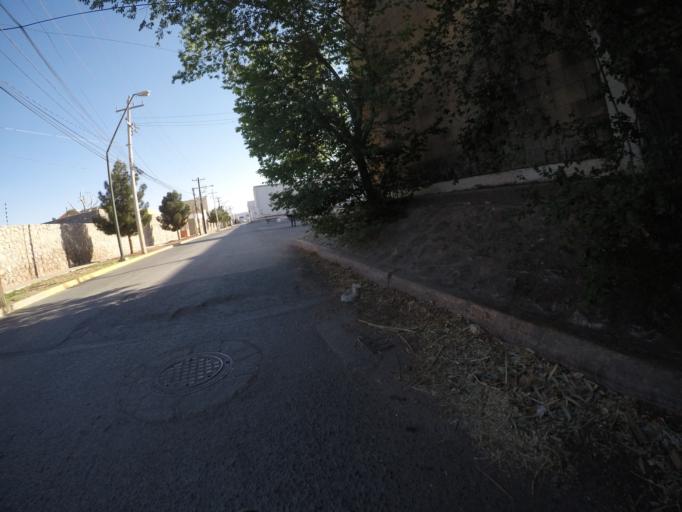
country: MX
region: Chihuahua
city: Ciudad Juarez
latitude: 31.7032
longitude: -106.3982
